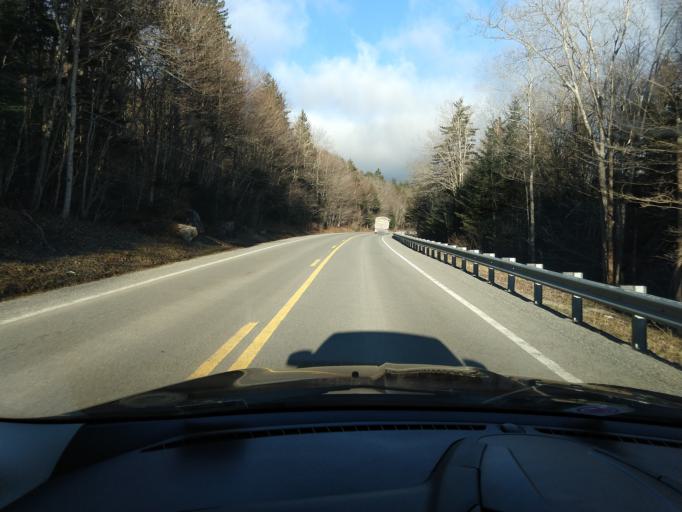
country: US
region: West Virginia
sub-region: Randolph County
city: Elkins
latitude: 38.6074
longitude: -79.8636
